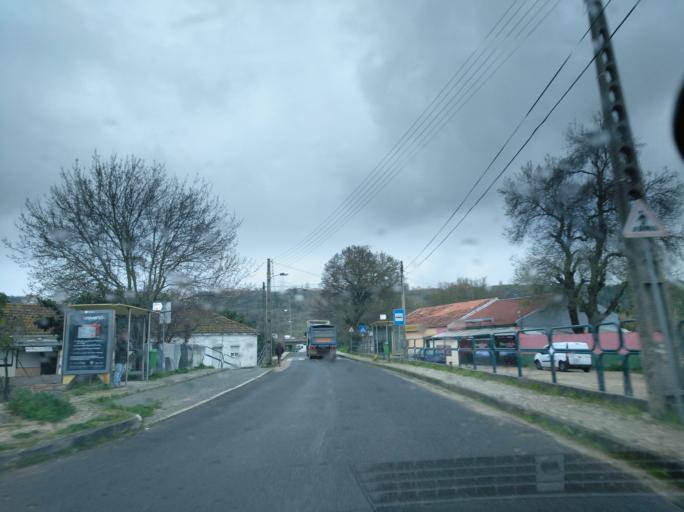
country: PT
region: Lisbon
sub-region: Odivelas
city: Pontinha
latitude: 38.7767
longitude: -9.1983
